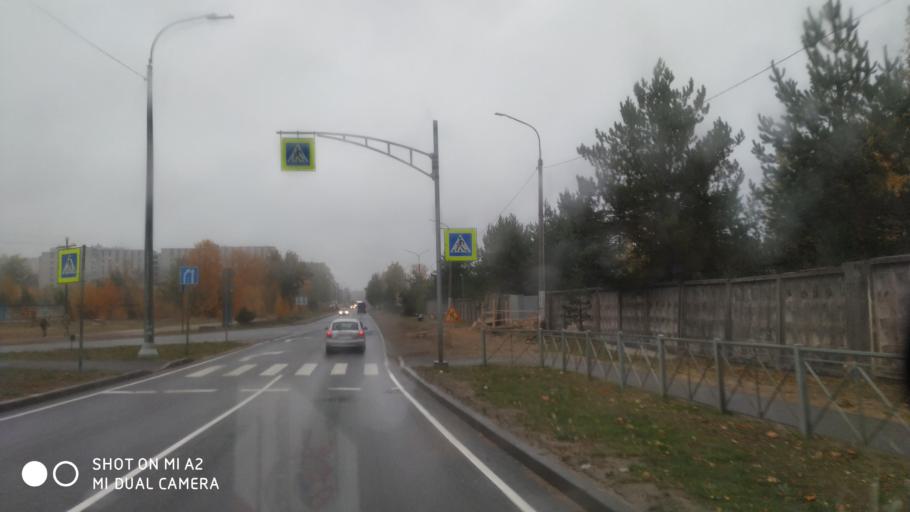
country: RU
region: Leningrad
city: Sosnovyy Bor
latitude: 59.8841
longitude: 29.0978
